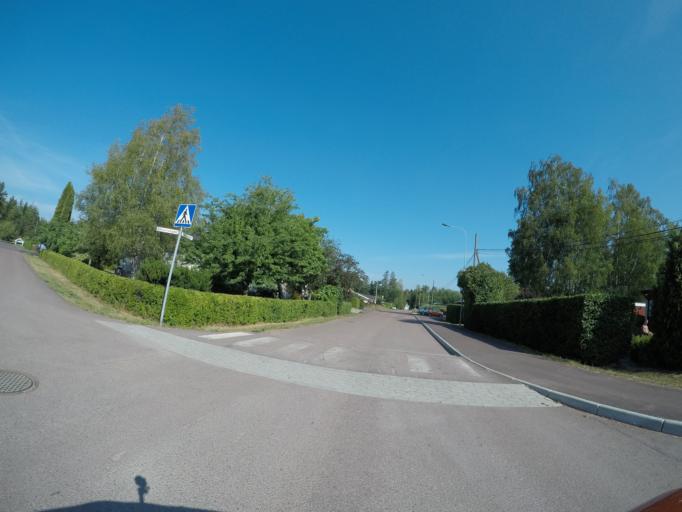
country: AX
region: Alands landsbygd
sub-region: Finstroem
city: Finstroem
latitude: 60.2269
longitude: 19.9791
